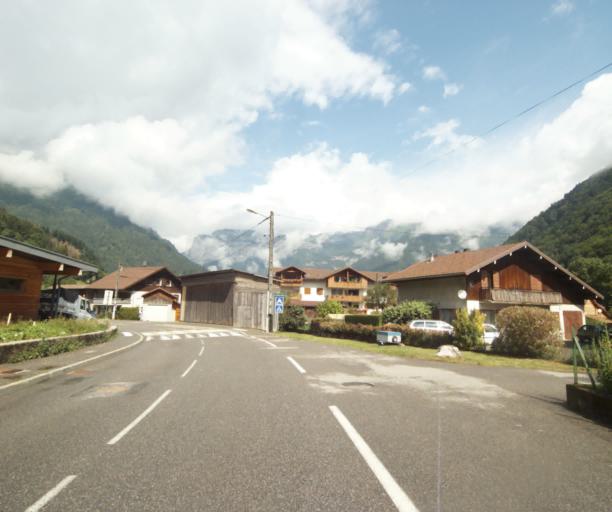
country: FR
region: Rhone-Alpes
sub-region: Departement de la Haute-Savoie
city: Thones
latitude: 45.8827
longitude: 6.3165
